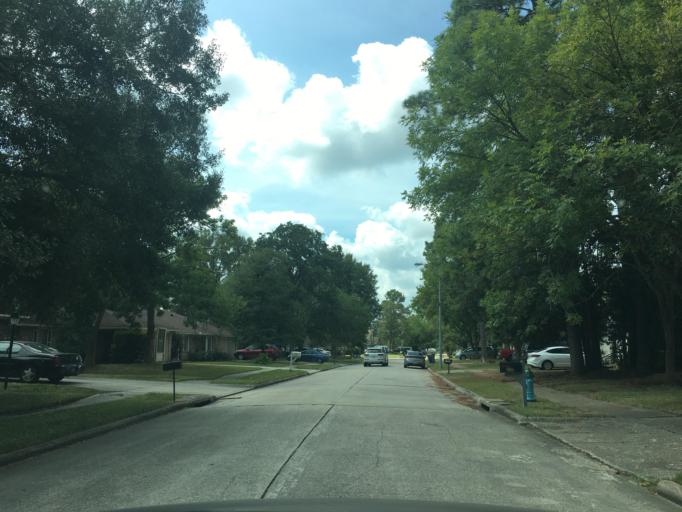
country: US
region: Texas
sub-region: Harris County
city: Spring
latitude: 30.1164
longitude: -95.4011
